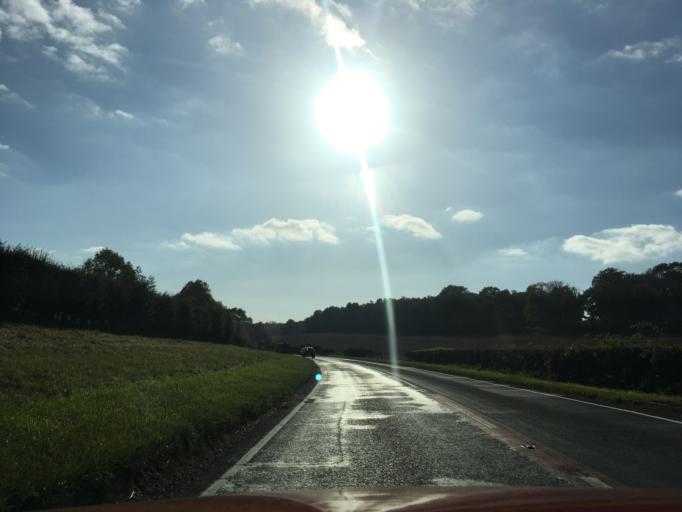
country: GB
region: England
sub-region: Hampshire
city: Four Marks
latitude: 51.0782
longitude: -1.0084
